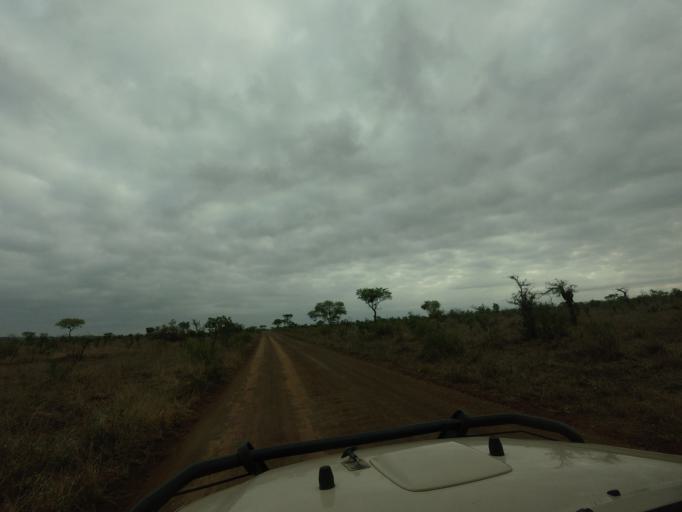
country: ZA
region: Mpumalanga
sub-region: Ehlanzeni District
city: Komatipoort
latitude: -25.3096
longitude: 31.9139
